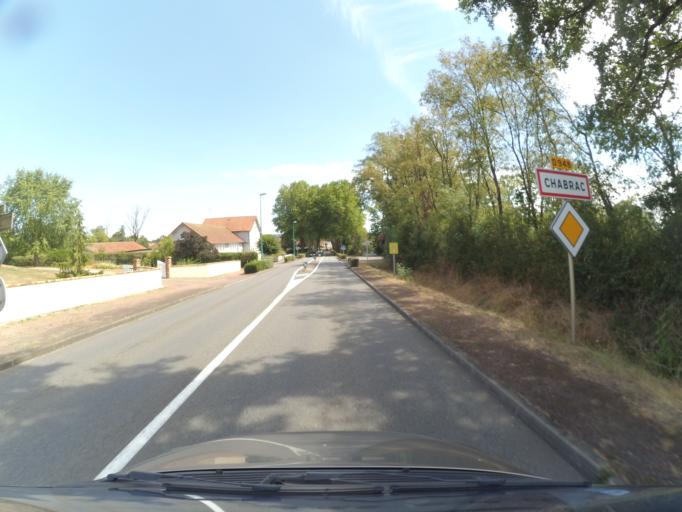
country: FR
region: Poitou-Charentes
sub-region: Departement de la Charente
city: Etagnac
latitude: 45.9350
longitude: 0.7366
